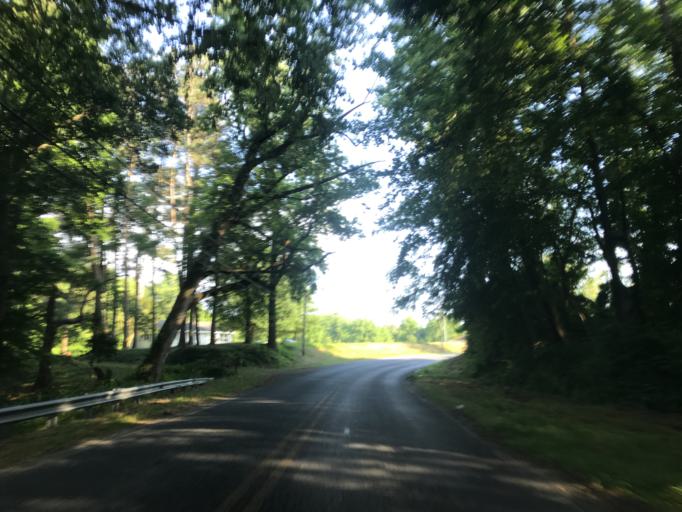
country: US
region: Maryland
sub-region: Caroline County
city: Federalsburg
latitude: 38.7106
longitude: -75.7765
